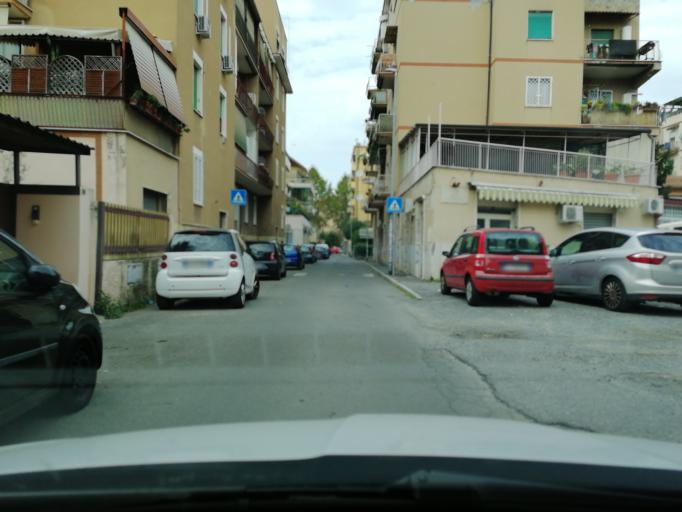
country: IT
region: Latium
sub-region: Citta metropolitana di Roma Capitale
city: Rome
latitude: 41.8599
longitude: 12.5488
